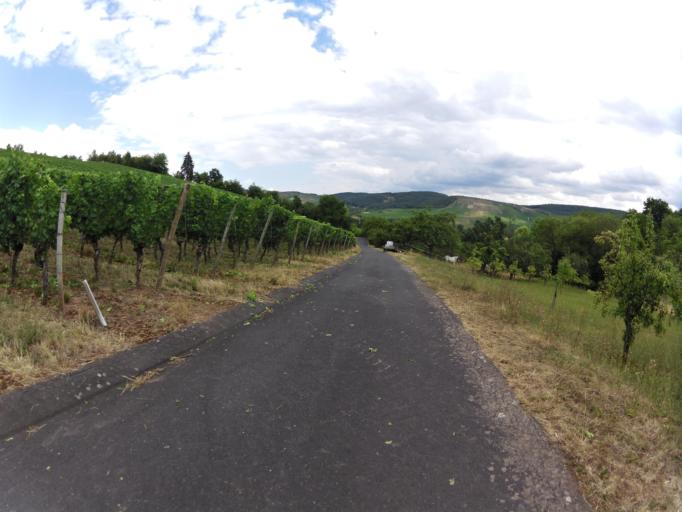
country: DE
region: Bavaria
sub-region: Regierungsbezirk Unterfranken
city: Erlabrunn
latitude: 49.8684
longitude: 9.8325
